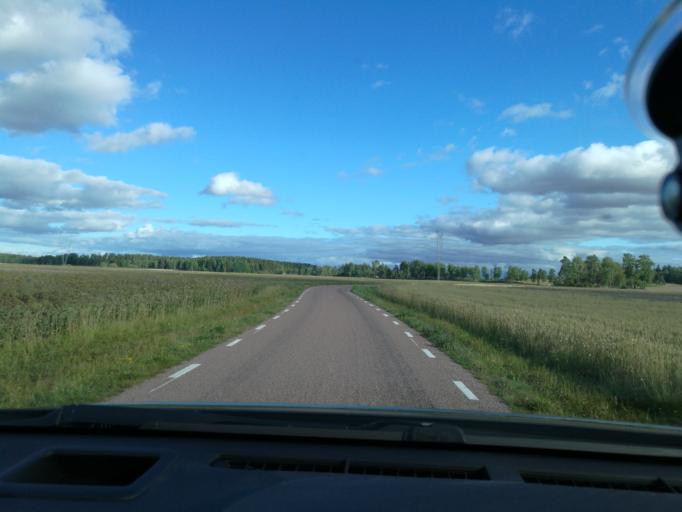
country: SE
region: Vaestmanland
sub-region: Kopings Kommun
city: Koping
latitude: 59.5542
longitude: 16.1042
